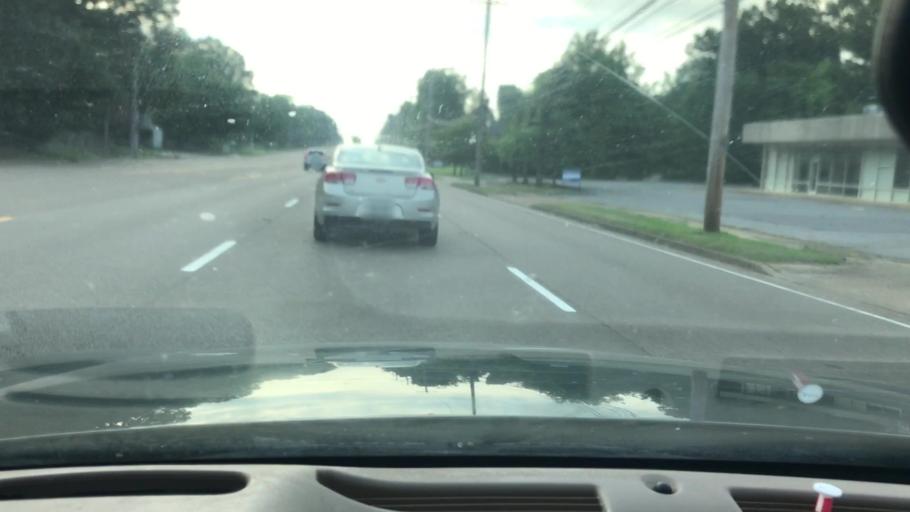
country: US
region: Tennessee
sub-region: Shelby County
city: Bartlett
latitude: 35.2048
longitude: -89.8525
